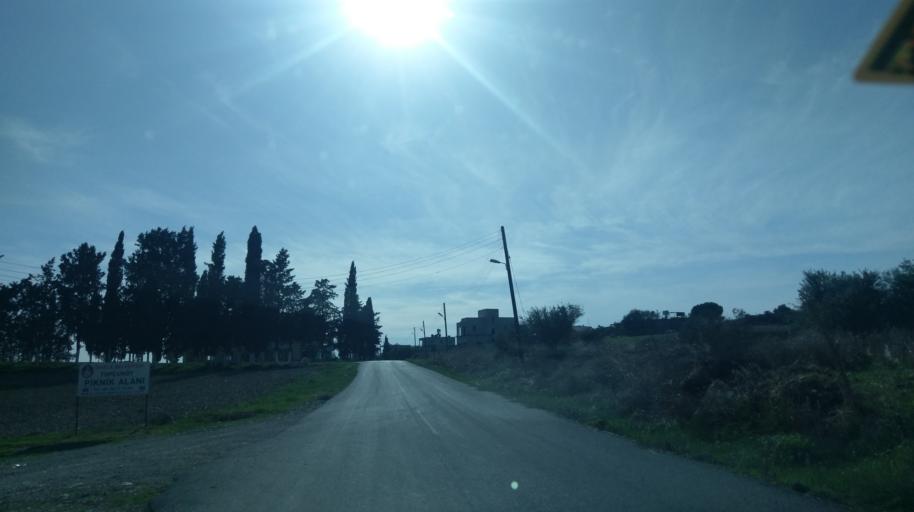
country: CY
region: Ammochostos
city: Trikomo
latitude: 35.3433
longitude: 33.8756
